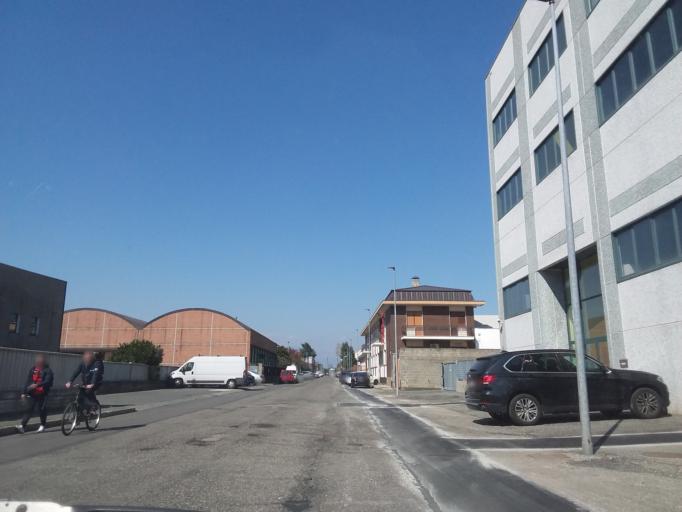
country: IT
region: Piedmont
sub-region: Provincia di Torino
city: Collegno
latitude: 45.0770
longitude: 7.5571
